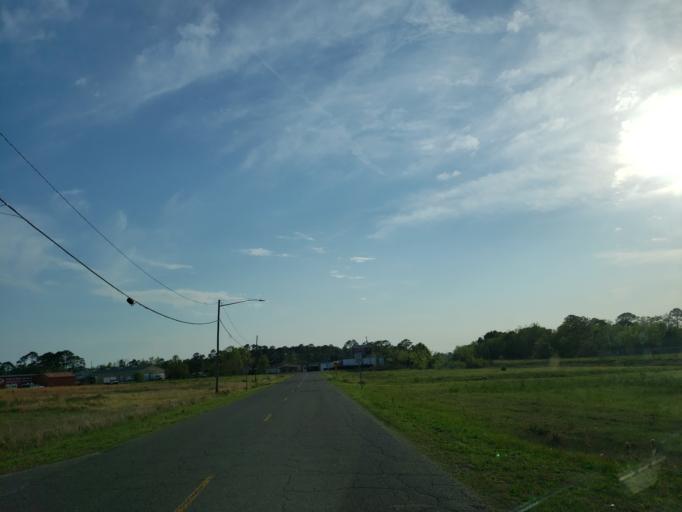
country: US
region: Mississippi
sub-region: Harrison County
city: West Gulfport
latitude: 30.3944
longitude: -89.0590
